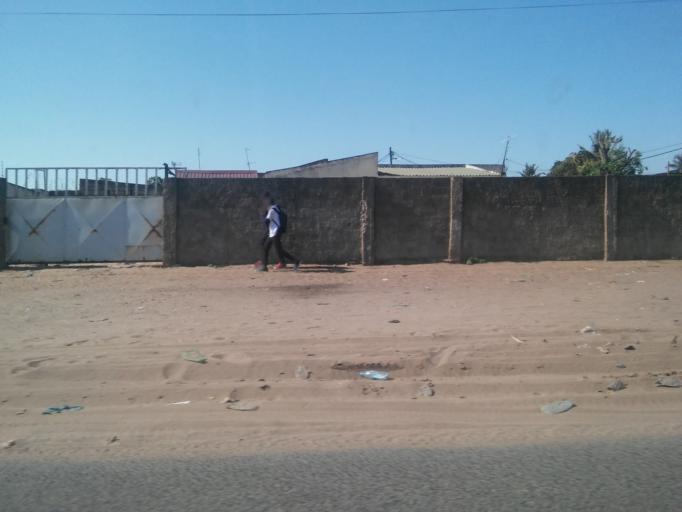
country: MZ
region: Maputo City
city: Maputo
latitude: -25.8566
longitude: 32.5672
